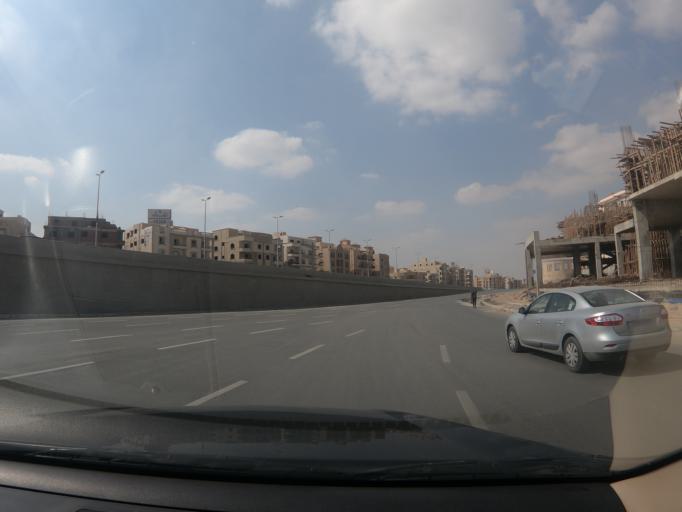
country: EG
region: Muhafazat al Qalyubiyah
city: Al Khankah
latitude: 30.0293
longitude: 31.4757
